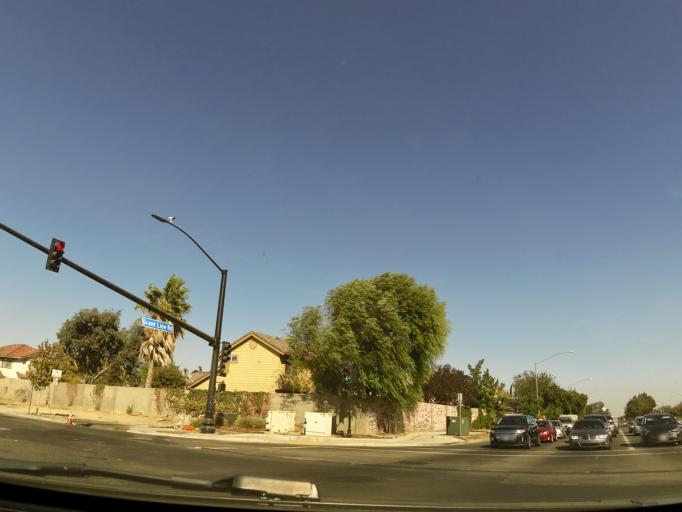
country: US
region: California
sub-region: San Joaquin County
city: Tracy
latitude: 37.7542
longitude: -121.4528
